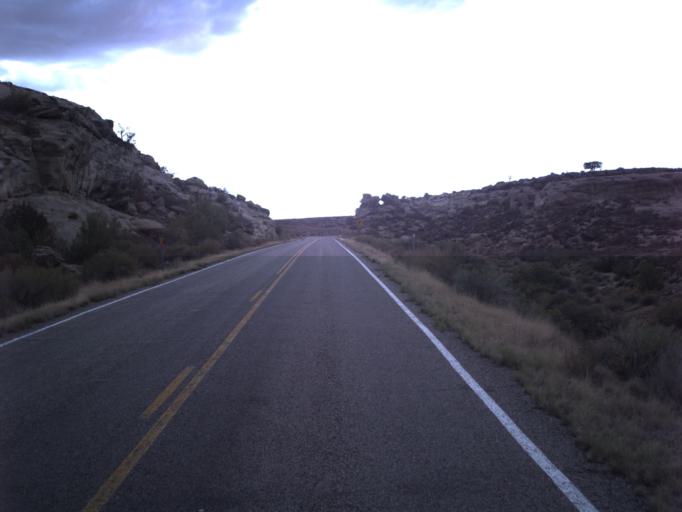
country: US
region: Utah
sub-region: San Juan County
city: Blanding
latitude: 37.4186
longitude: -109.4472
